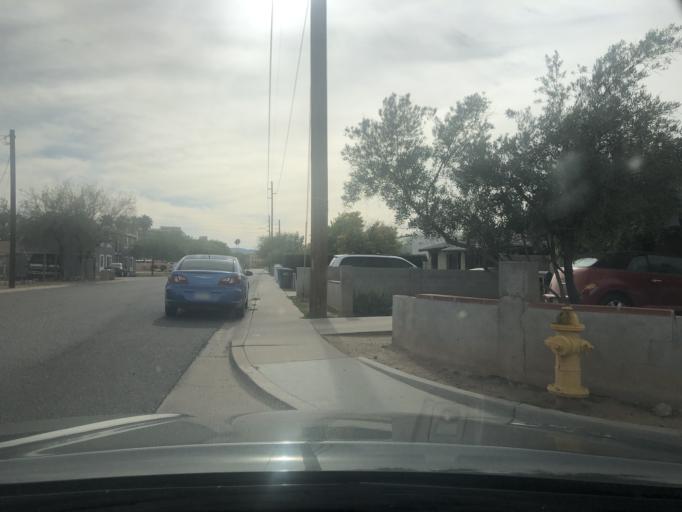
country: US
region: Arizona
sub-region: Maricopa County
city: Phoenix
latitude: 33.4604
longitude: -112.0433
